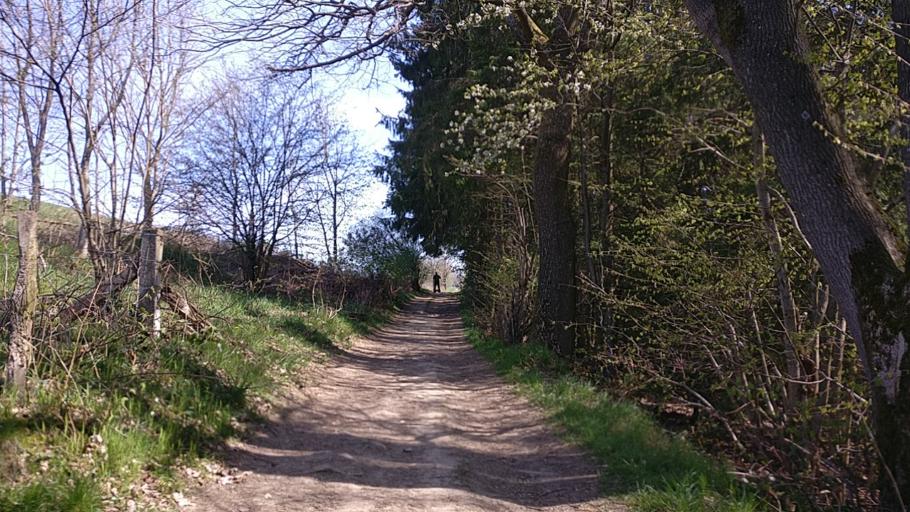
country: DE
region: Rheinland-Pfalz
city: Asbach
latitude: 50.6575
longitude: 7.4262
